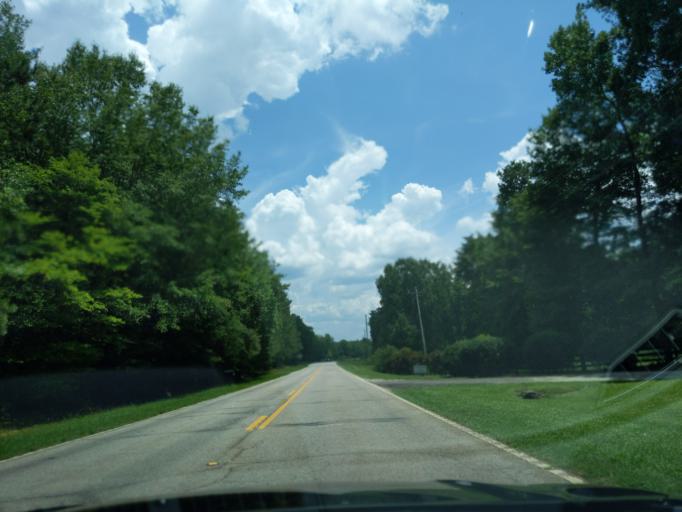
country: US
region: South Carolina
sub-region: Edgefield County
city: Edgefield
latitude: 33.8675
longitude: -81.9911
